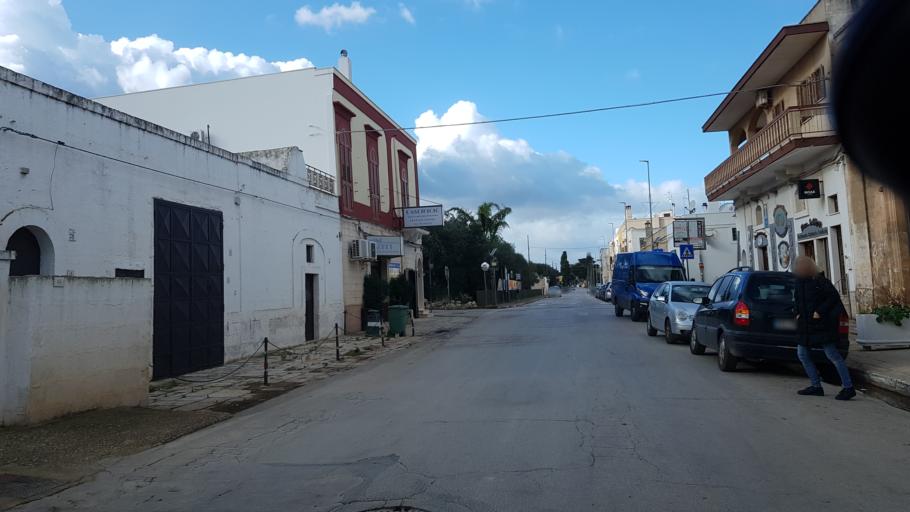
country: IT
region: Apulia
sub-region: Provincia di Brindisi
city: Montalbano
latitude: 40.7910
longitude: 17.4612
